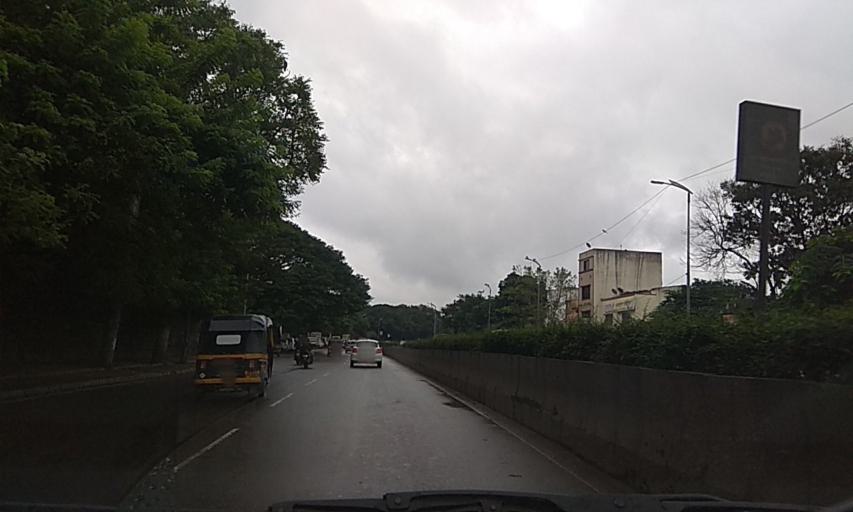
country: IN
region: Maharashtra
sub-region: Pune Division
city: Khadki
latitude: 18.5532
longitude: 73.8815
